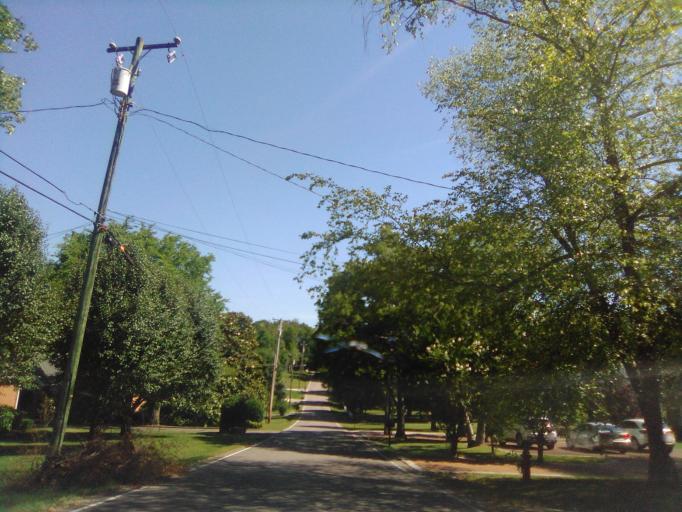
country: US
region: Tennessee
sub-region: Davidson County
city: Belle Meade
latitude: 36.1174
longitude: -86.8332
